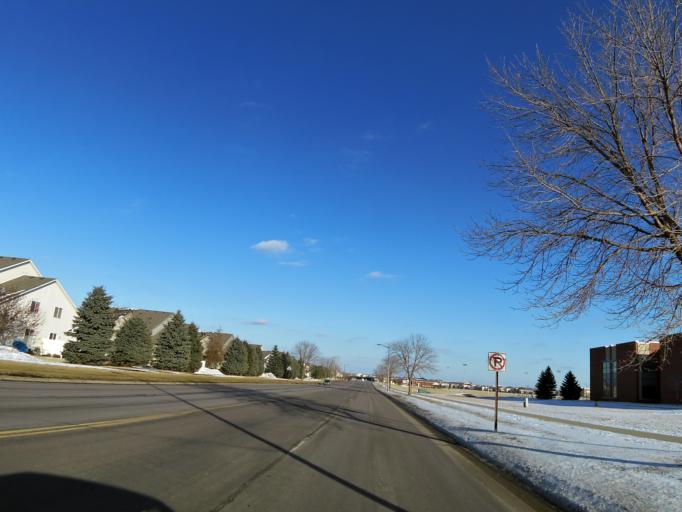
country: US
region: Minnesota
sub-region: Scott County
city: Shakopee
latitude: 44.7737
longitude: -93.4940
